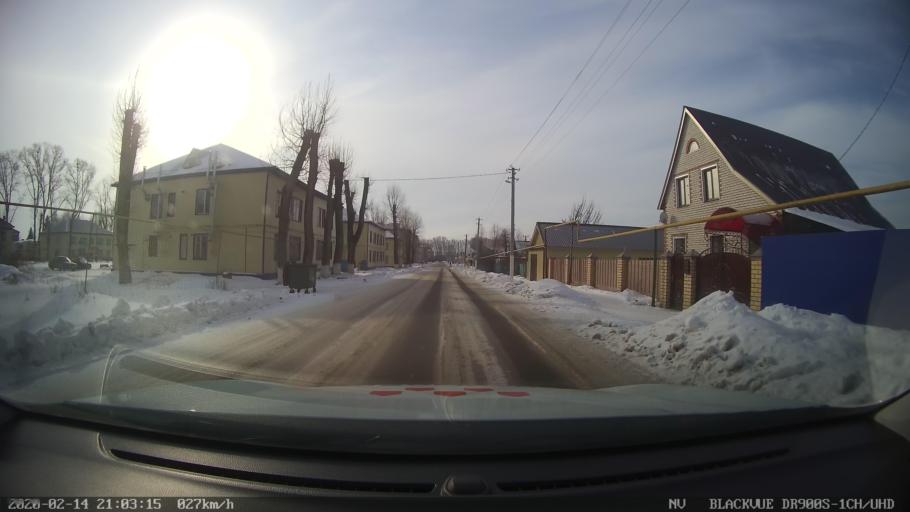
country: RU
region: Tatarstan
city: Kuybyshevskiy Zaton
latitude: 55.1575
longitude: 49.1764
